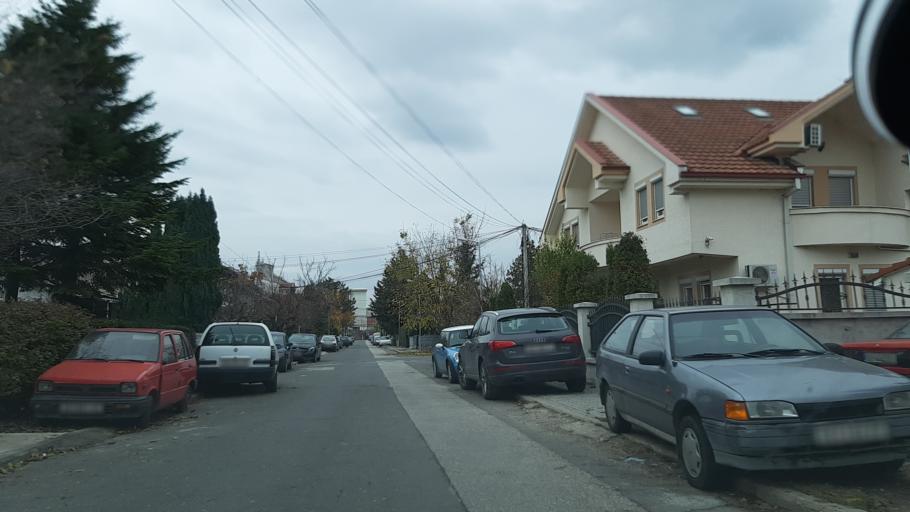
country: MK
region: Kisela Voda
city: Usje
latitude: 41.9744
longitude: 21.4670
